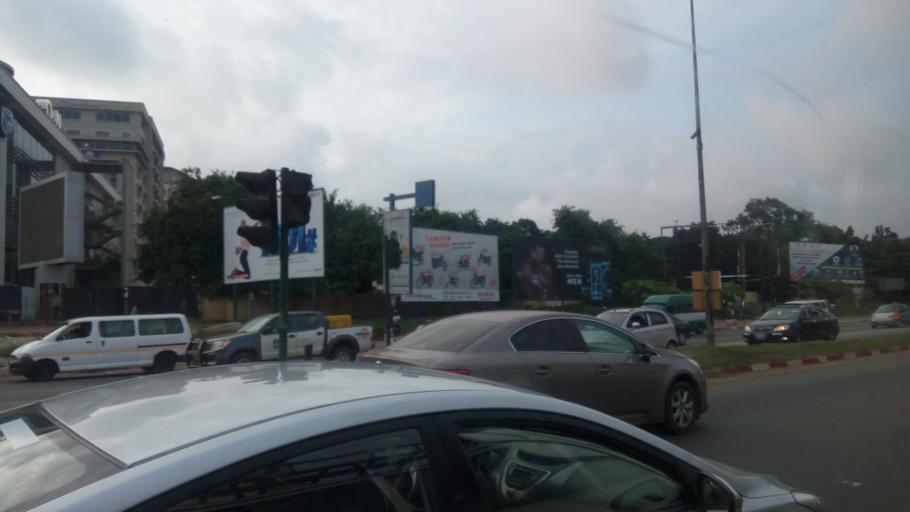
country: GH
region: Greater Accra
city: Accra
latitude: 5.6000
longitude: -0.1785
